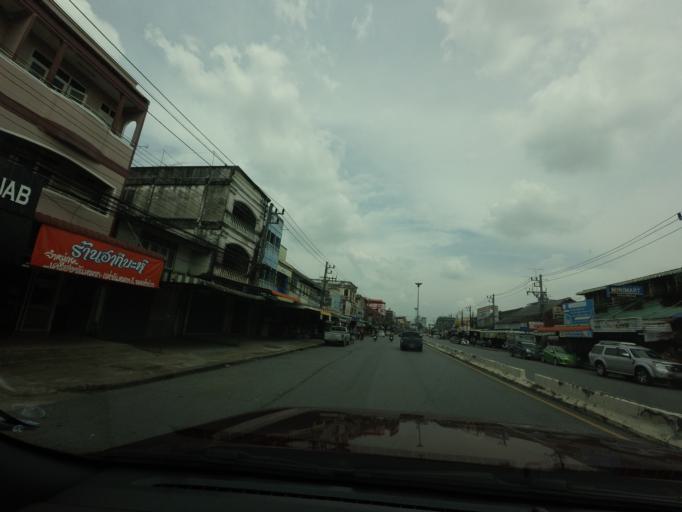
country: TH
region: Yala
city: Yala
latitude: 6.5653
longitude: 101.2945
